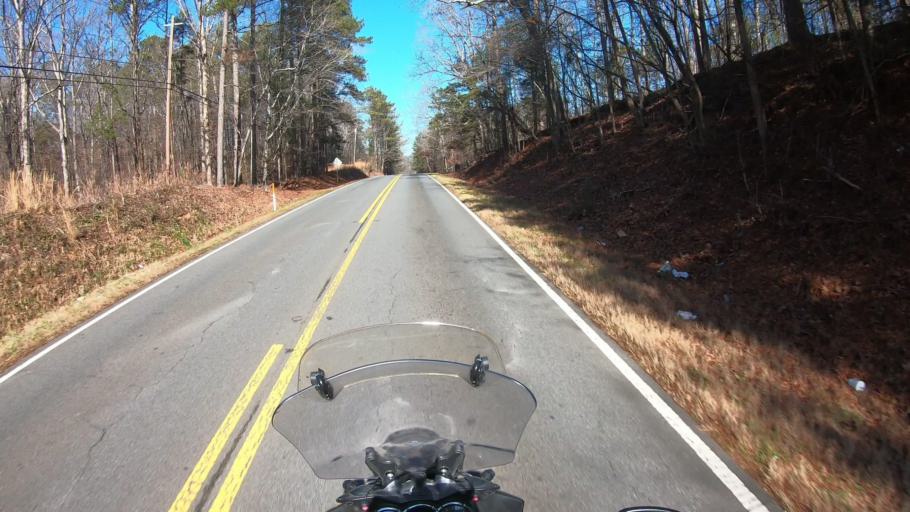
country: US
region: Georgia
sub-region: Bartow County
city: Cartersville
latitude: 34.2535
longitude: -84.8087
